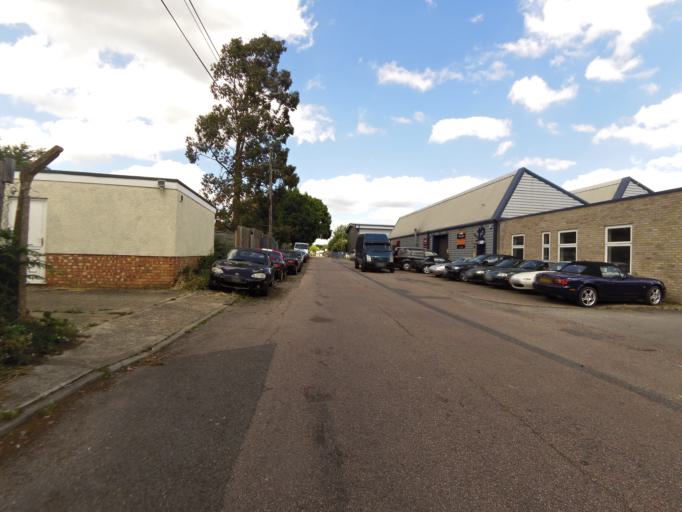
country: GB
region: England
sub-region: Suffolk
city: Kesgrave
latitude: 52.0360
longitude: 1.1985
